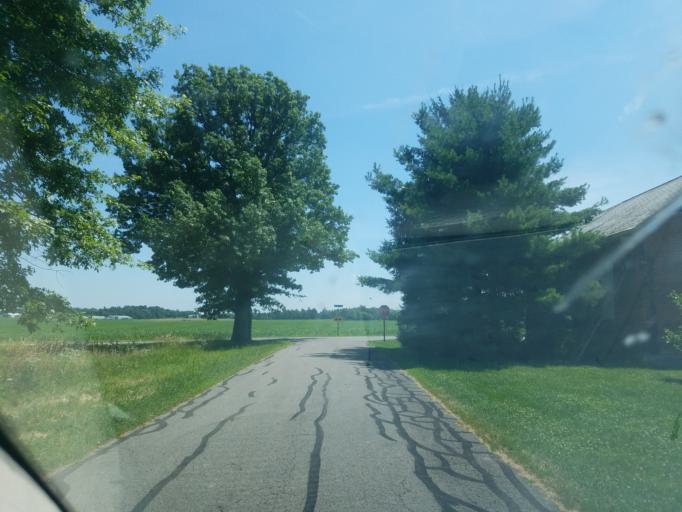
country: US
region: Ohio
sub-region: Hancock County
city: Arlington
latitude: 40.8632
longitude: -83.7089
